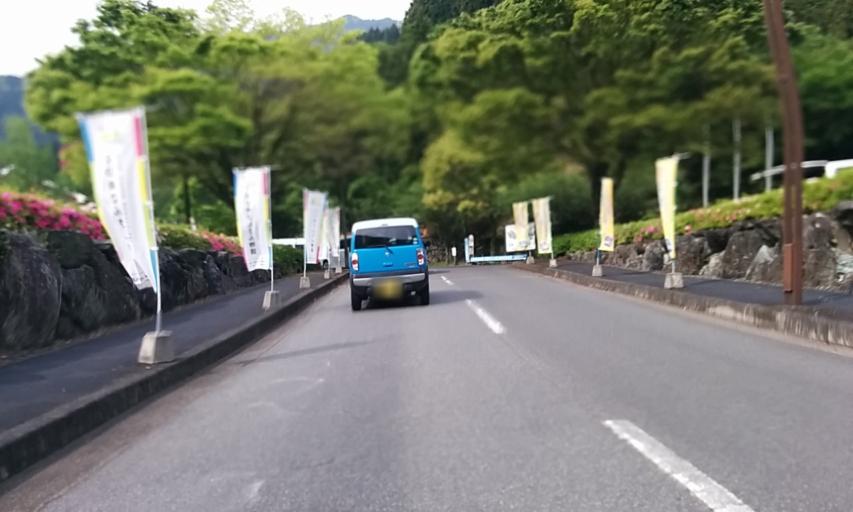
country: JP
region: Ehime
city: Niihama
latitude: 33.9030
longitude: 133.3103
